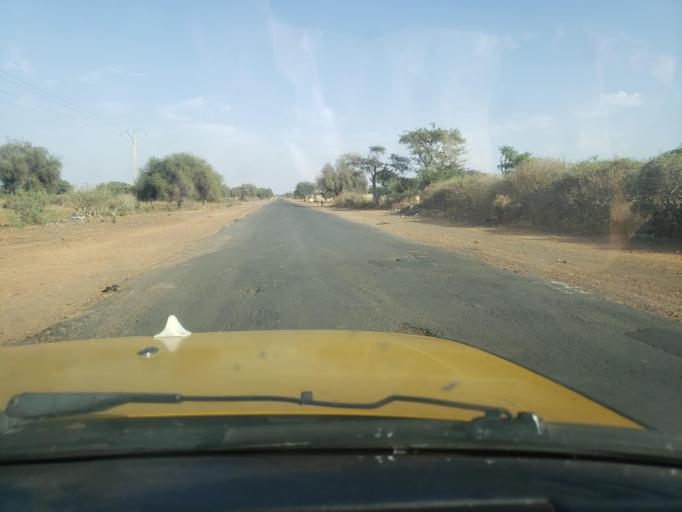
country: SN
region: Louga
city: Louga
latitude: 15.5018
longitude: -15.9421
